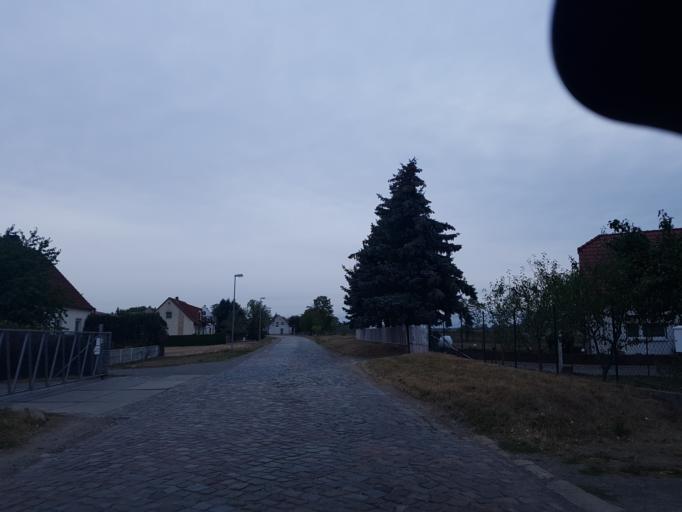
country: DE
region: Saxony
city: Belgern
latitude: 51.4942
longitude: 13.1816
